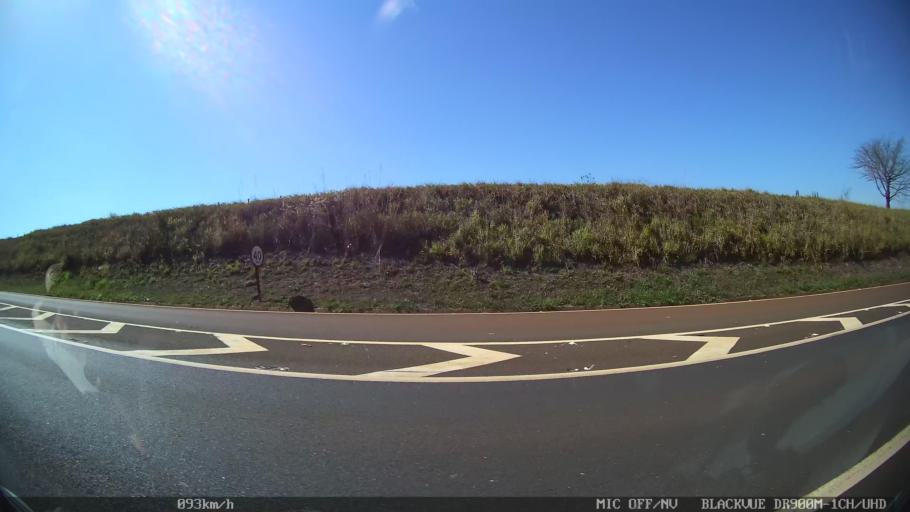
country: BR
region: Sao Paulo
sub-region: Batatais
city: Batatais
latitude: -20.7546
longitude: -47.5314
